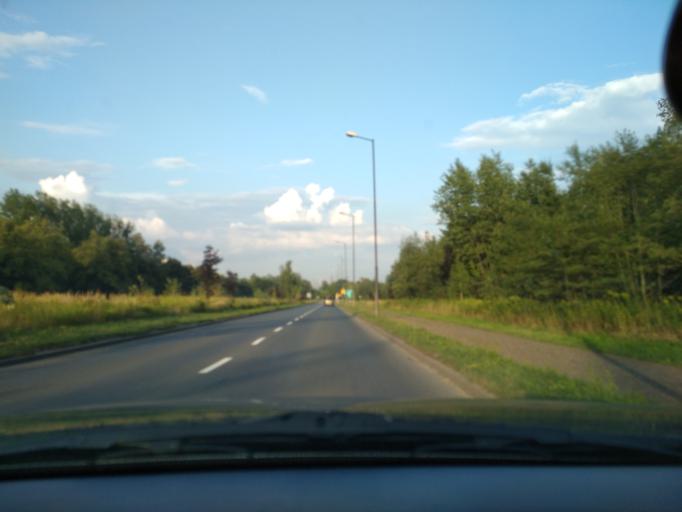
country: PL
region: Silesian Voivodeship
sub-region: Gliwice
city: Gliwice
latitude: 50.2713
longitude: 18.6974
